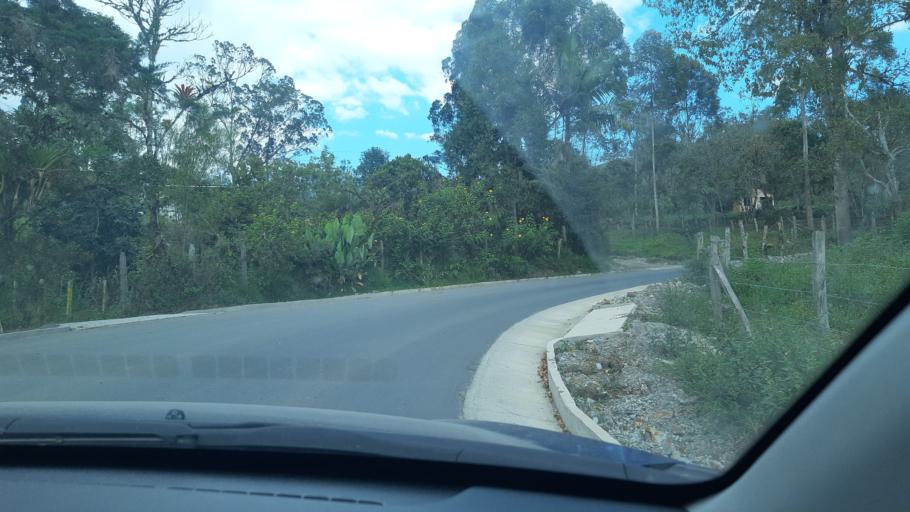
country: CO
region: Boyaca
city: Garagoa
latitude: 5.0893
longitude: -73.3454
